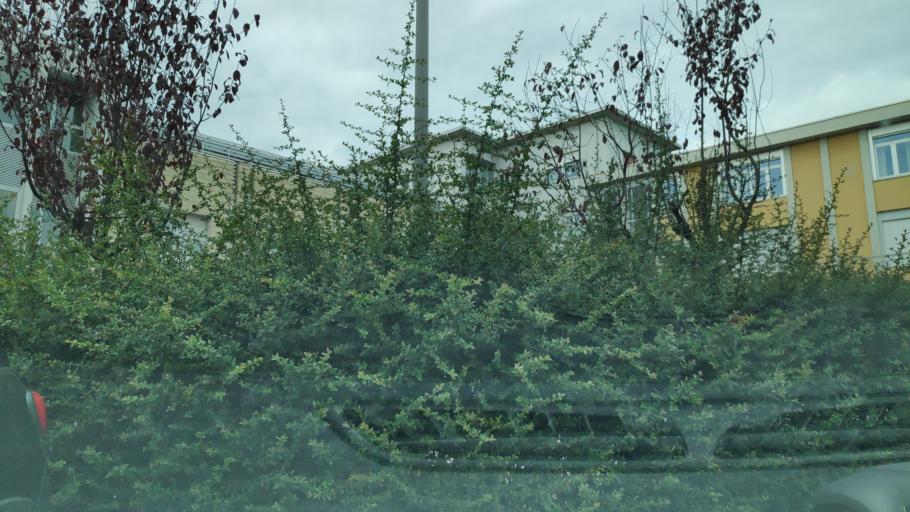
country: IT
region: Lombardy
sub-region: Provincia di Bergamo
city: Bergamo
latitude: 45.6874
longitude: 9.6757
